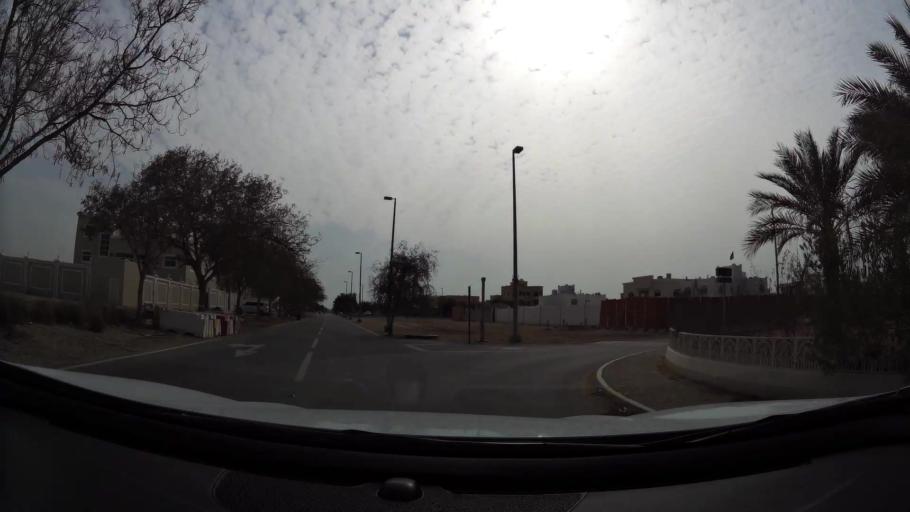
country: AE
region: Abu Dhabi
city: Abu Dhabi
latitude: 24.6017
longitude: 54.7018
